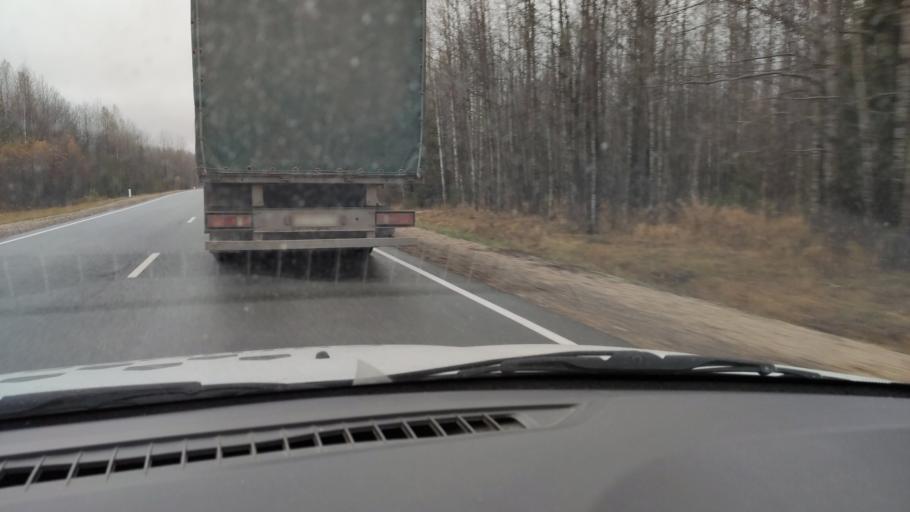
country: RU
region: Kirov
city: Chernaya Kholunitsa
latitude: 58.8023
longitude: 51.8577
